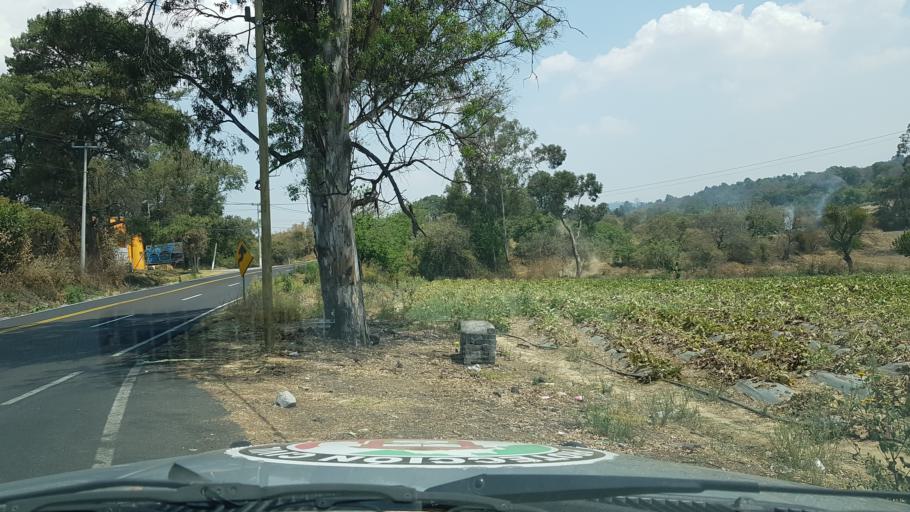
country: MX
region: Mexico
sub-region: Tepetlixpa
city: Nepantla de Sor Juana Ines de la Cruz
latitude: 18.9918
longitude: -98.8252
